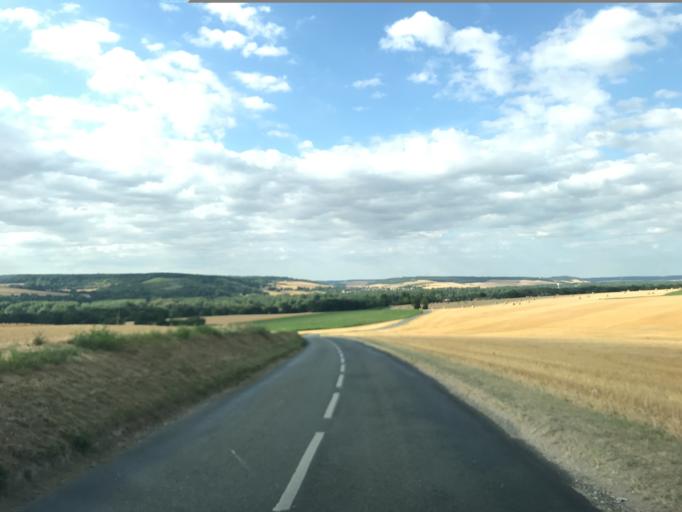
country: FR
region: Ile-de-France
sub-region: Departement des Yvelines
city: Freneuse
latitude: 49.0659
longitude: 1.5892
